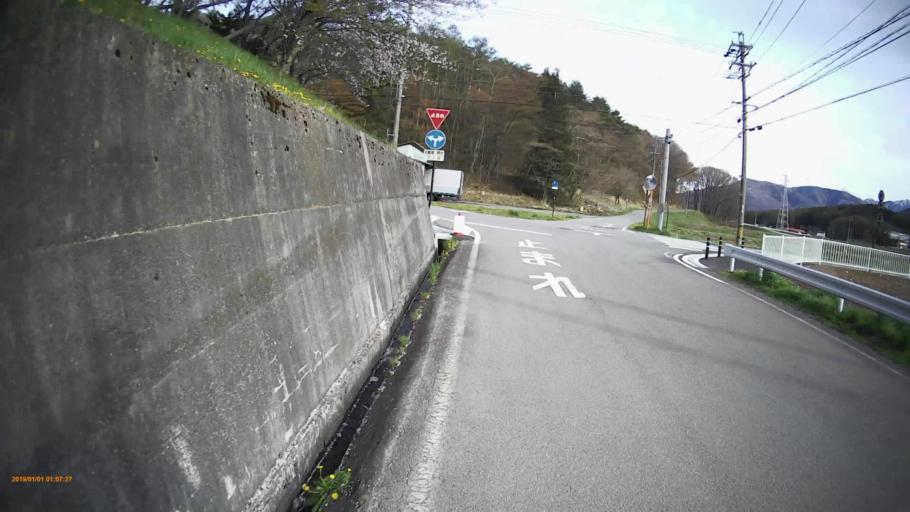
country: JP
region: Nagano
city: Chino
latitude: 35.9161
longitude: 138.2191
